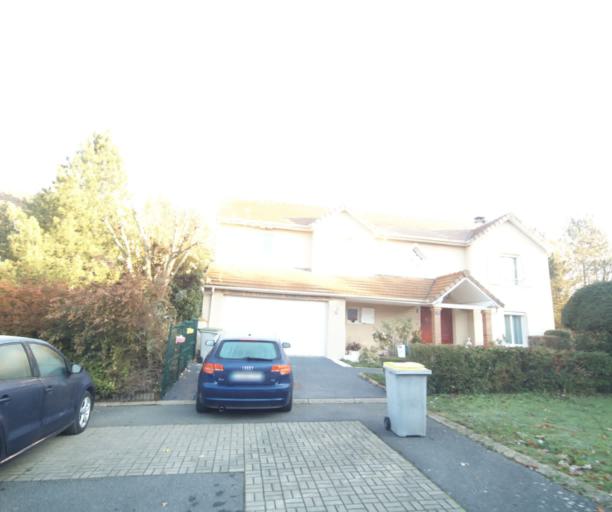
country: FR
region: Ile-de-France
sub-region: Departement du Val-d'Oise
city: Gonesse
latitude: 48.9944
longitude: 2.4343
